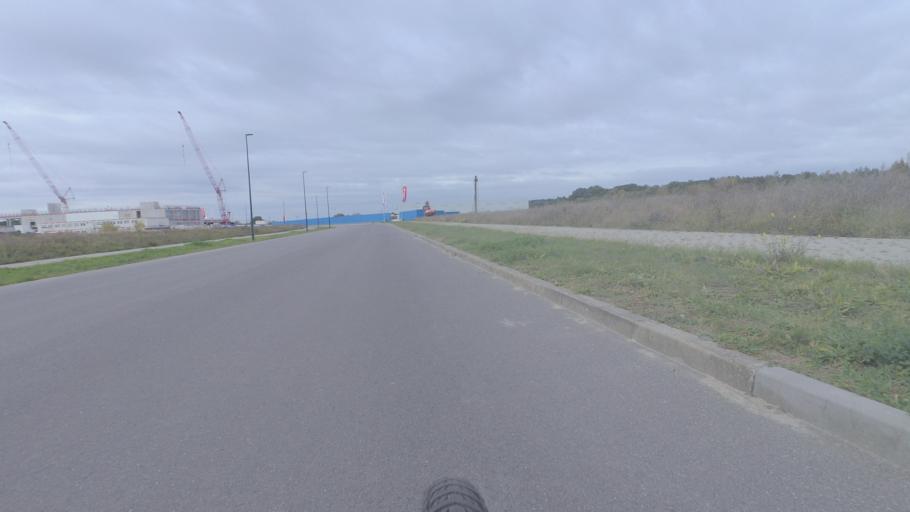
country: DE
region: Brandenburg
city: Grossbeeren
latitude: 52.3217
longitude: 13.2991
